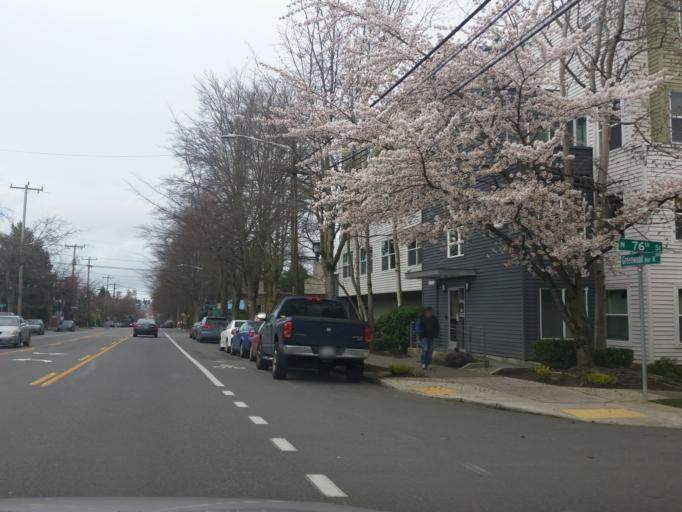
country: US
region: Washington
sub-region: King County
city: Shoreline
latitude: 47.6839
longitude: -122.3552
